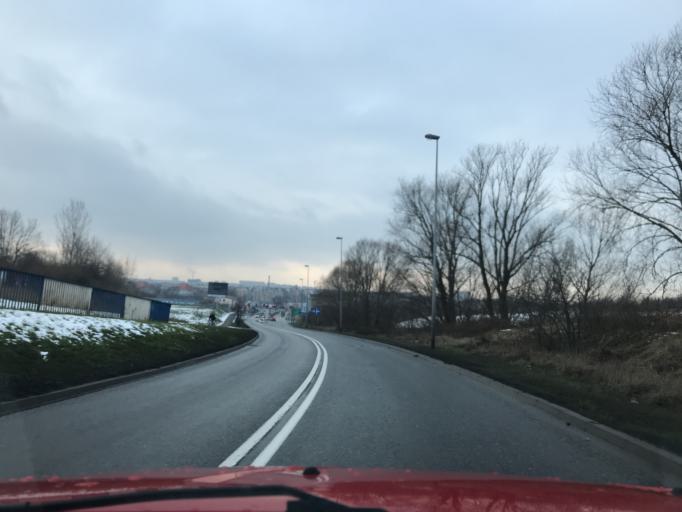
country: PL
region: Greater Poland Voivodeship
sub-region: Kalisz
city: Kalisz
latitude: 51.7724
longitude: 18.0977
